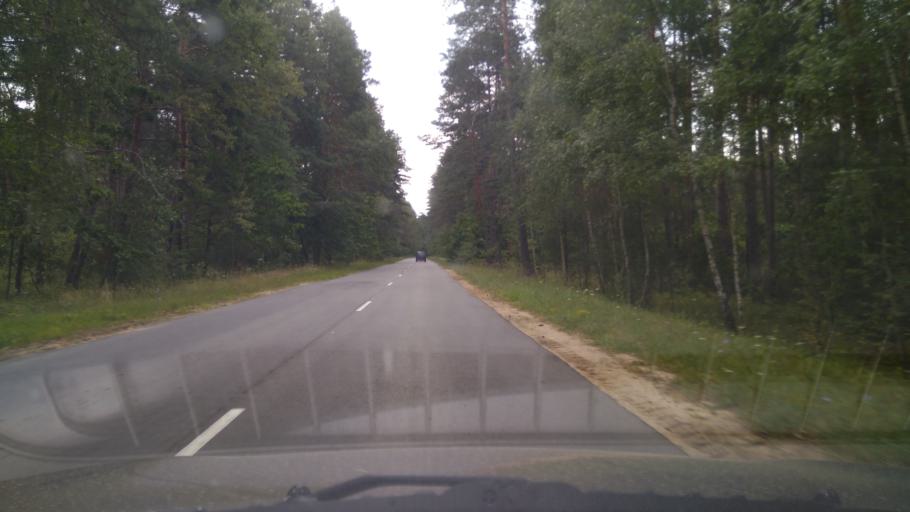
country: BY
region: Brest
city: Nyakhachava
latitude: 52.6006
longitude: 25.0953
